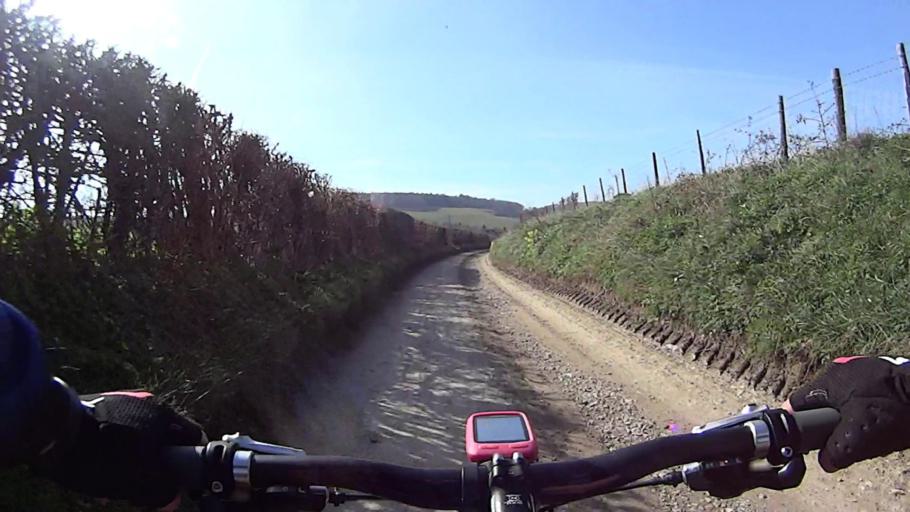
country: GB
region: England
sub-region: West Sussex
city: Boxgrove
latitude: 50.9131
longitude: -0.7361
